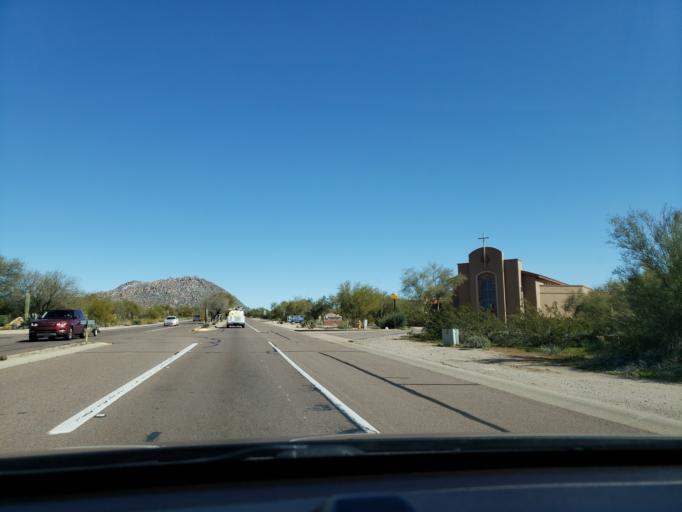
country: US
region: Arizona
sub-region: Maricopa County
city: Carefree
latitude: 33.7126
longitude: -111.8832
